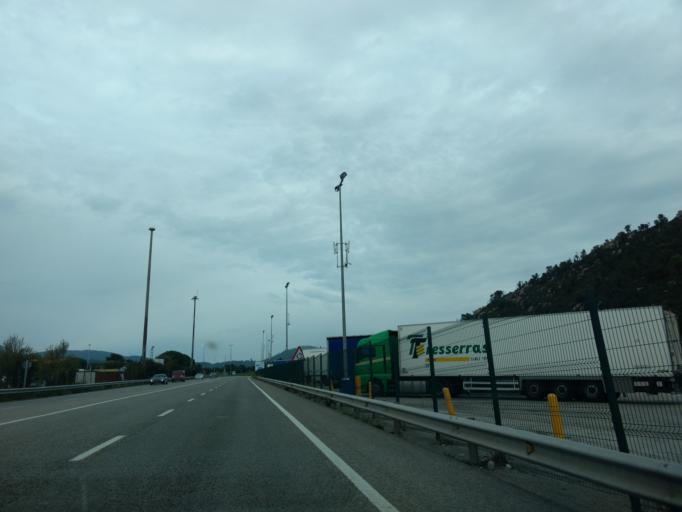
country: ES
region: Catalonia
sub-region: Provincia de Girona
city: la Jonquera
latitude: 42.4312
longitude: 2.8669
